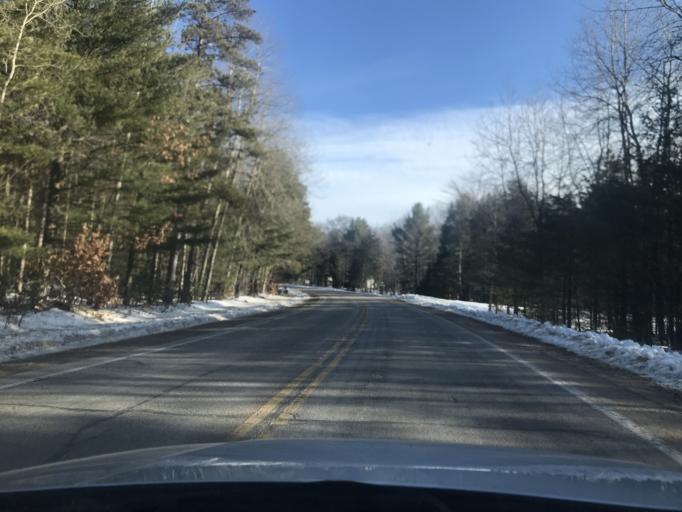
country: US
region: Wisconsin
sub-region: Marinette County
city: Peshtigo
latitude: 45.0324
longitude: -87.7182
